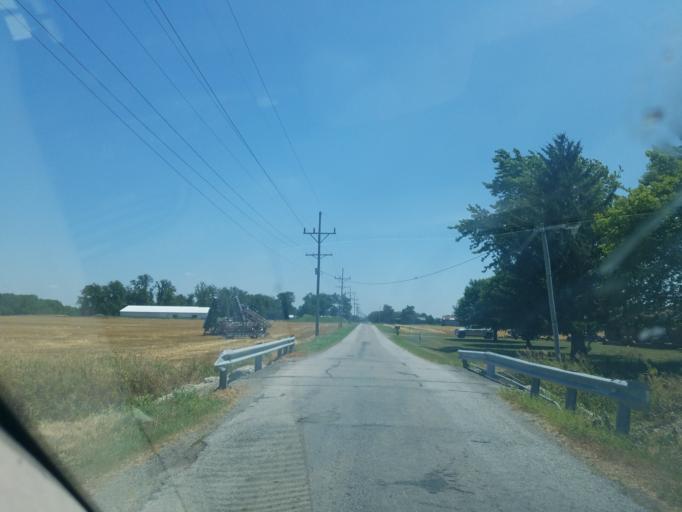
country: US
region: Ohio
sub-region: Allen County
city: Delphos
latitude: 40.7794
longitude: -84.3246
